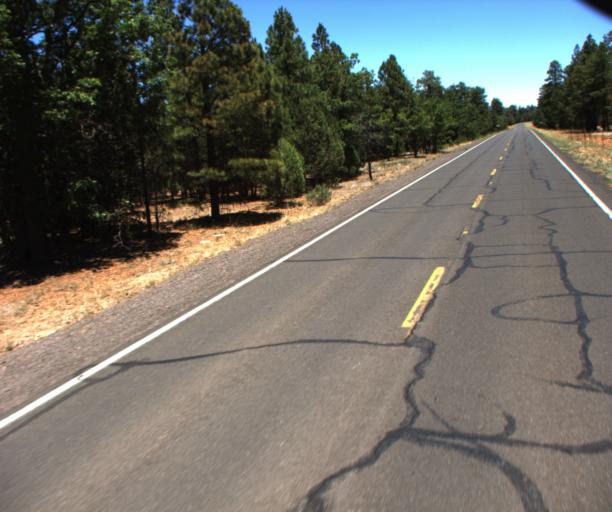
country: US
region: Arizona
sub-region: Gila County
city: Pine
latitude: 34.6201
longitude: -111.1711
